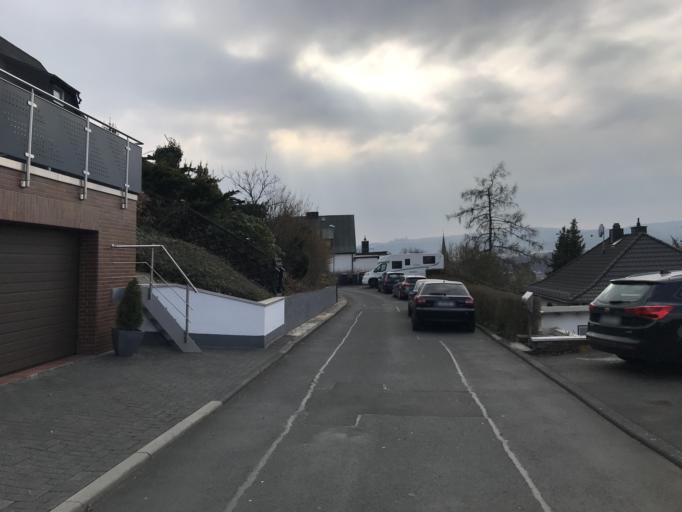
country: DE
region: Hesse
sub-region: Regierungsbezirk Giessen
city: Sinn
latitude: 50.6555
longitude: 8.3339
